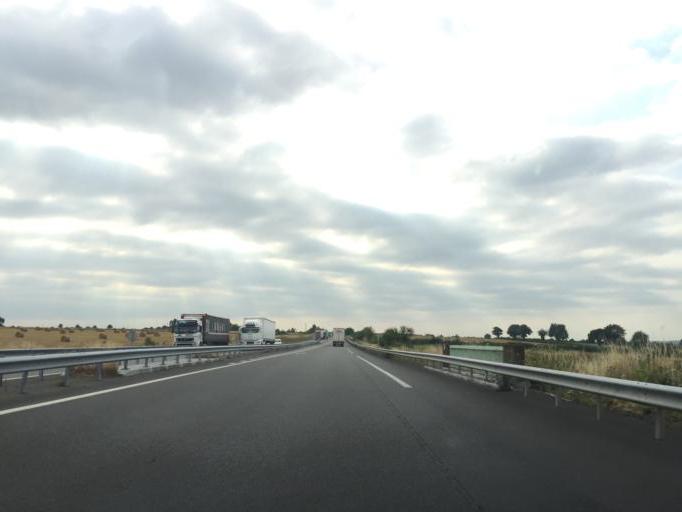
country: FR
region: Auvergne
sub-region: Departement de l'Allier
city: Diou
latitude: 46.4904
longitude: 3.8148
